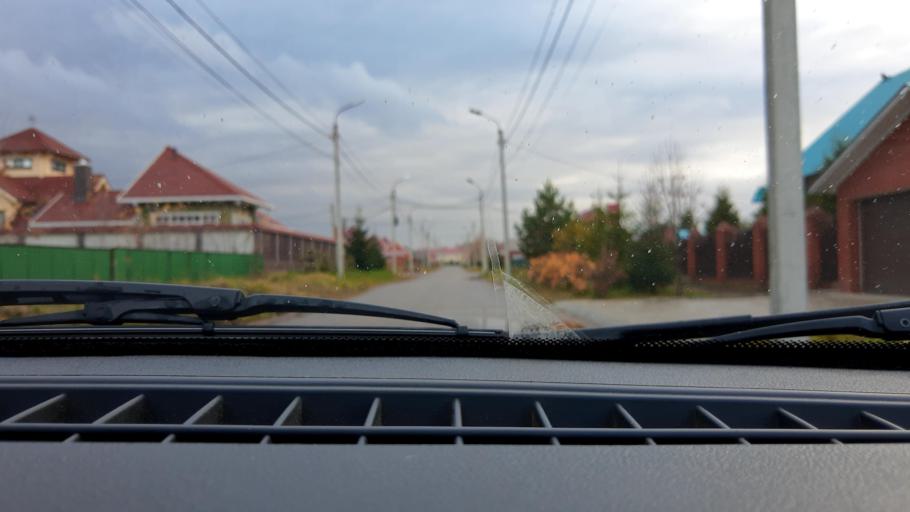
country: RU
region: Bashkortostan
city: Ufa
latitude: 54.8552
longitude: 56.0166
